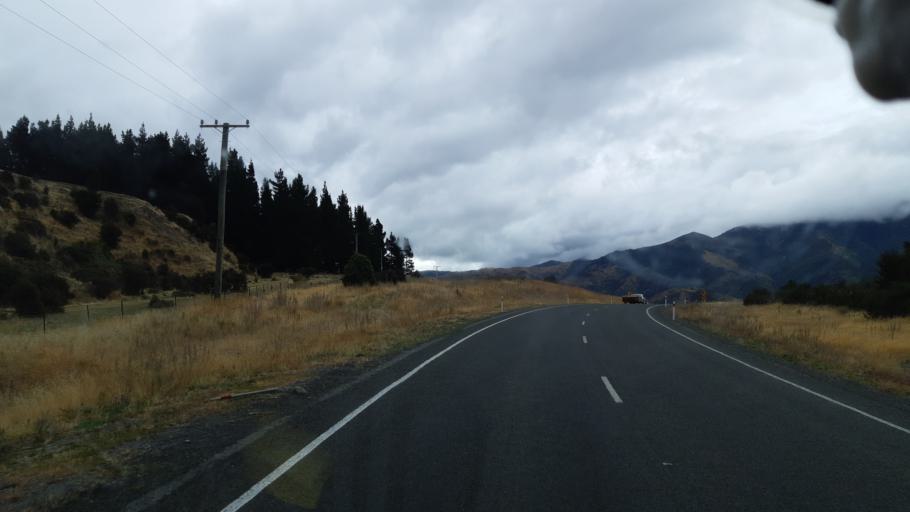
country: NZ
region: Canterbury
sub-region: Hurunui District
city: Amberley
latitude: -42.5723
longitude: 172.7124
